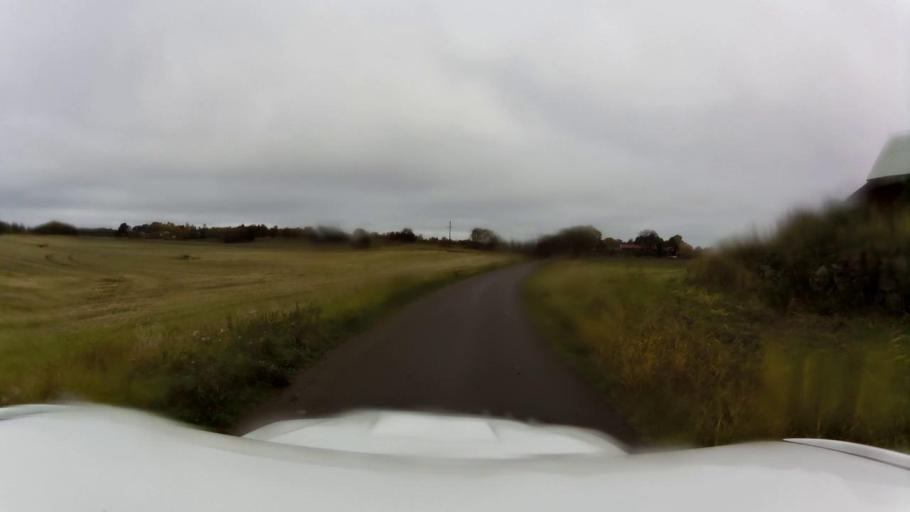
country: SE
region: OEstergoetland
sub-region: Linkopings Kommun
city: Linghem
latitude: 58.4888
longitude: 15.7427
